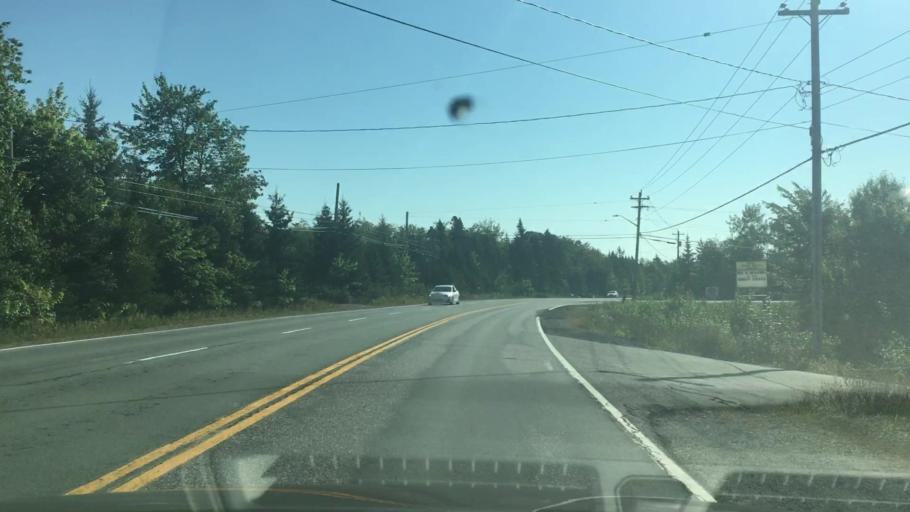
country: CA
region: Nova Scotia
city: Cole Harbour
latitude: 44.7791
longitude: -63.0794
